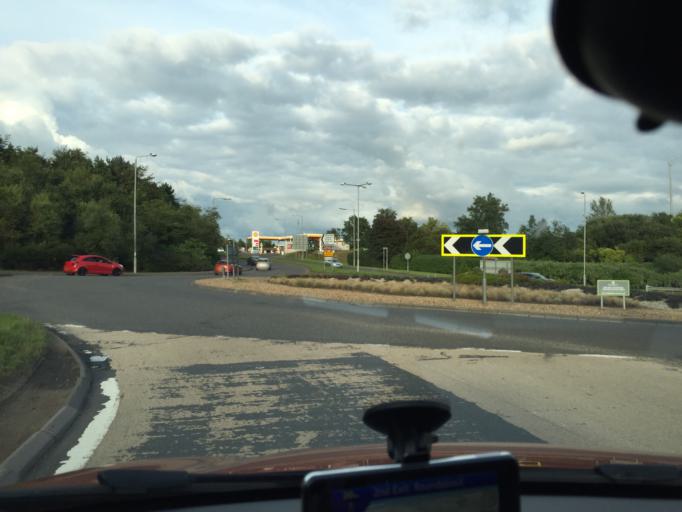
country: GB
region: Scotland
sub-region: North Lanarkshire
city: Cumbernauld
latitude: 55.9673
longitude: -3.9732
